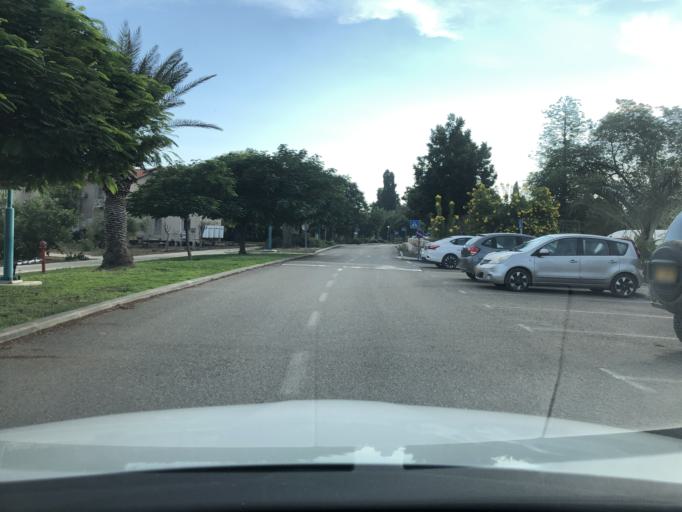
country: IL
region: Northern District
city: Yavne'el
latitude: 32.6625
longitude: 35.5837
